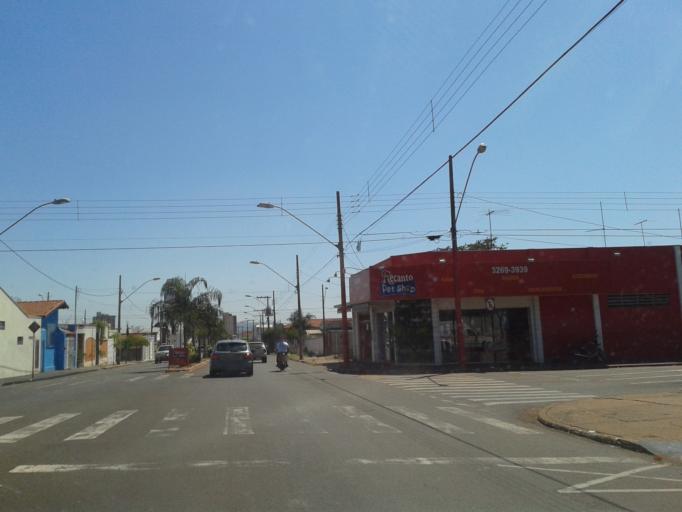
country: BR
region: Minas Gerais
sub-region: Ituiutaba
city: Ituiutaba
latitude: -18.9834
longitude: -49.4578
